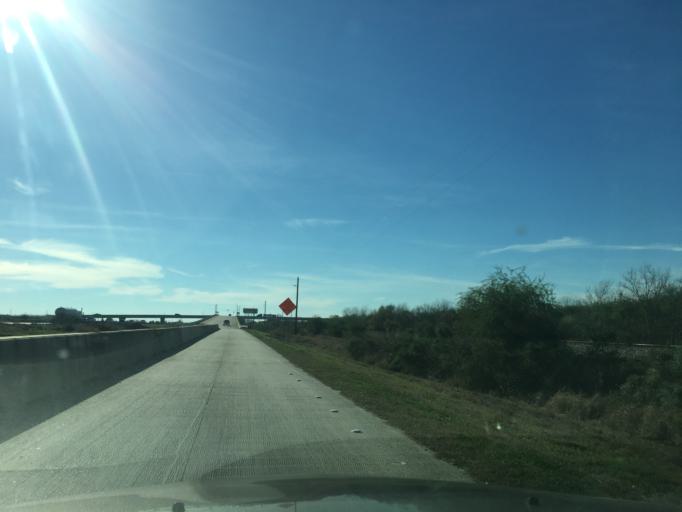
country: US
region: Texas
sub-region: Fort Bend County
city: Rosenberg
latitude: 29.5271
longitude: -95.8700
